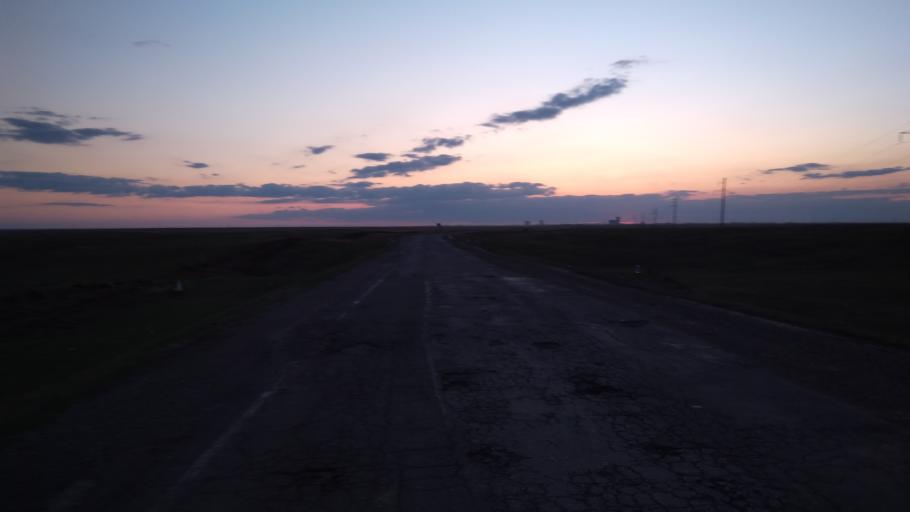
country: RU
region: Chelyabinsk
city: Troitsk
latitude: 54.0868
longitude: 61.6604
